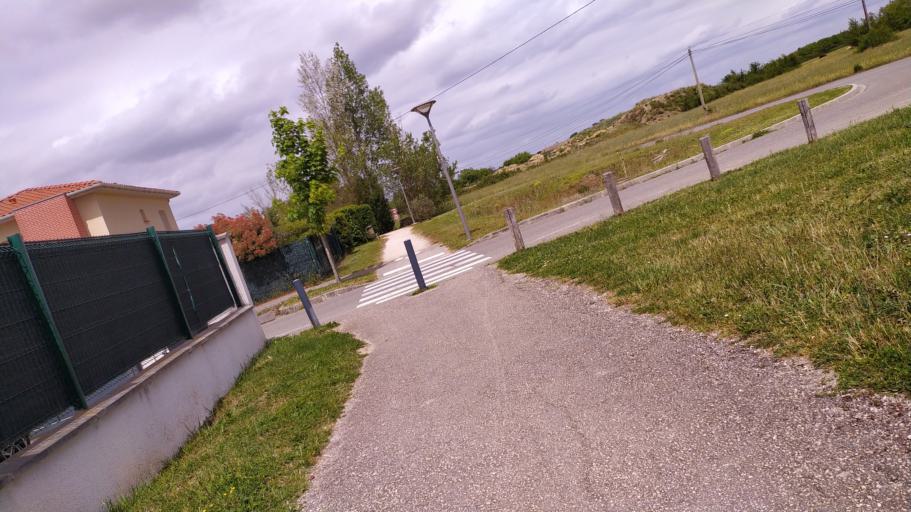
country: FR
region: Midi-Pyrenees
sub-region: Departement de la Haute-Garonne
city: La Salvetat-Saint-Gilles
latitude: 43.5821
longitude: 1.2893
